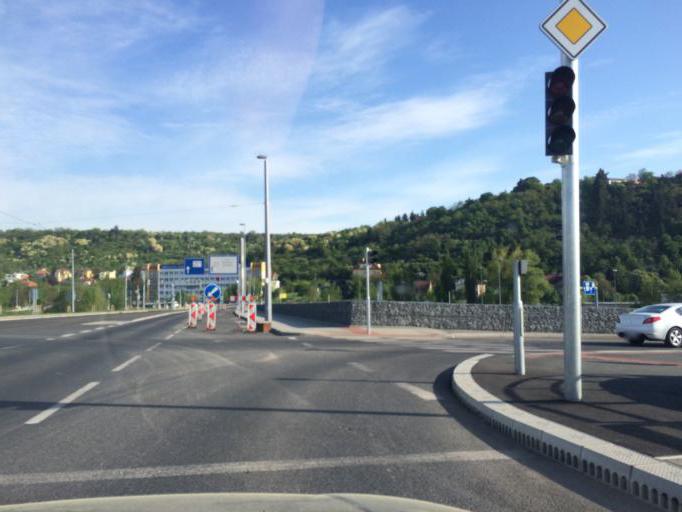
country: CZ
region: Praha
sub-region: Praha 8
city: Karlin
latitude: 50.1135
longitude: 14.4357
